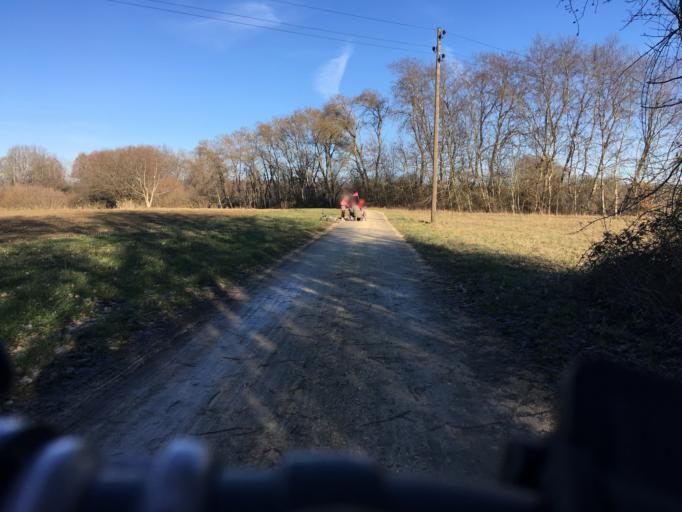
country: DE
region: Baden-Wuerttemberg
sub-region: Freiburg Region
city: Moos
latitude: 47.7171
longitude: 8.9142
